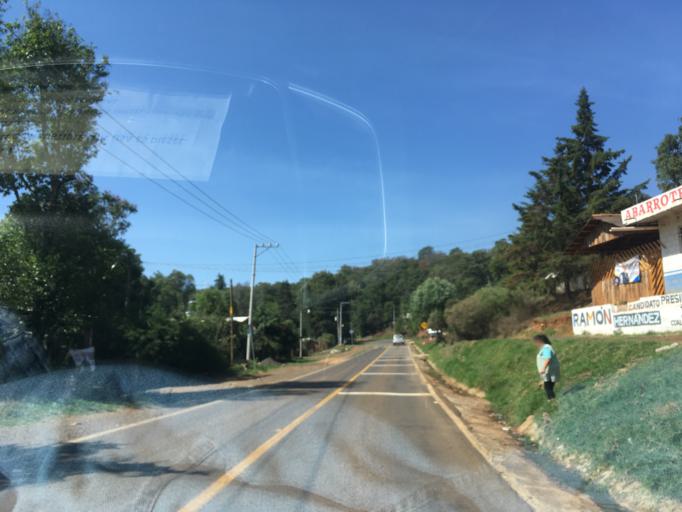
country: MX
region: Michoacan
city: Charo
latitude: 19.6704
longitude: -101.0061
